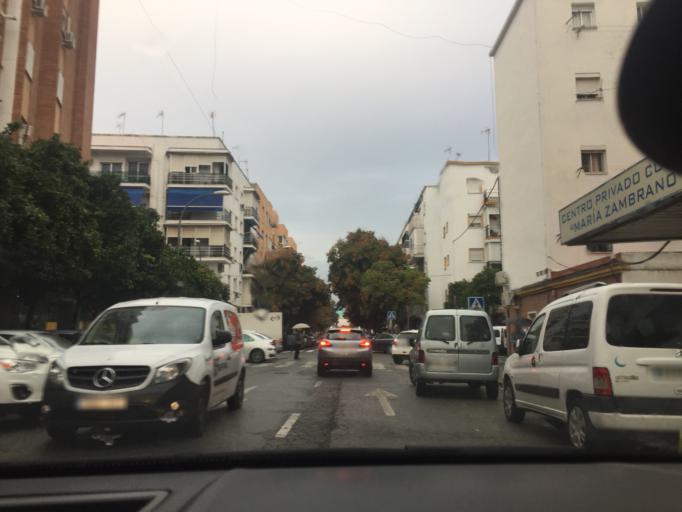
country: ES
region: Andalusia
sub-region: Provincia de Sevilla
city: Sevilla
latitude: 37.3958
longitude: -5.9776
